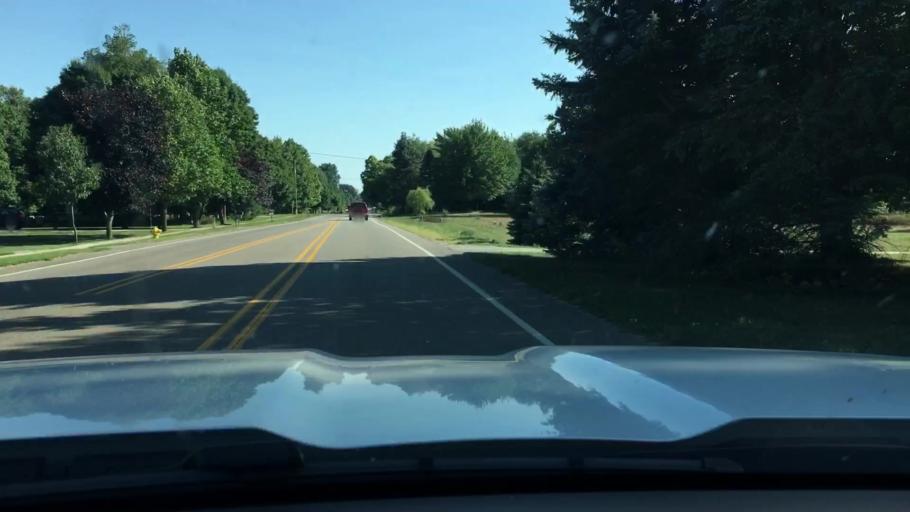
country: US
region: Michigan
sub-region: Ottawa County
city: Allendale
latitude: 42.9571
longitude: -85.9535
